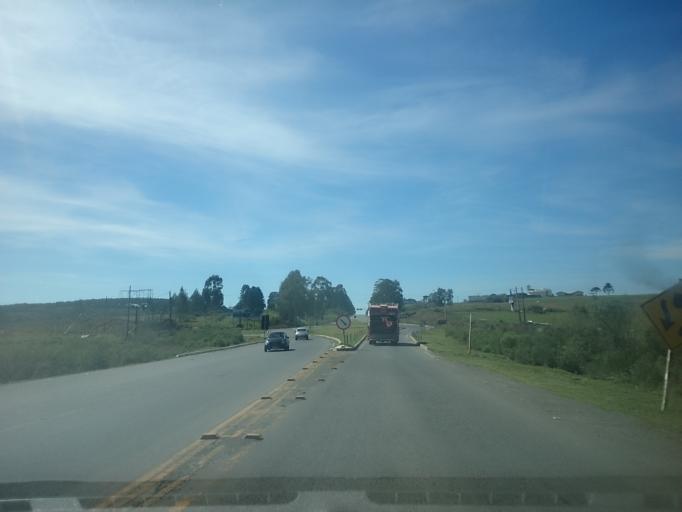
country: BR
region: Santa Catarina
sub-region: Lages
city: Lages
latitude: -27.7739
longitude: -50.2036
